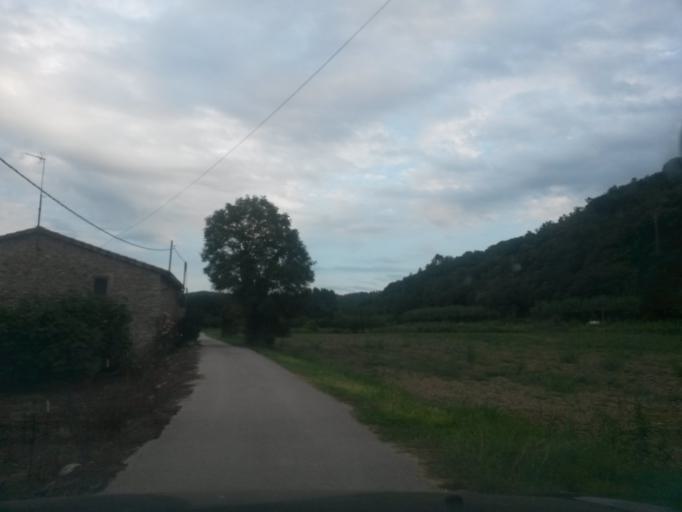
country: ES
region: Catalonia
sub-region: Provincia de Girona
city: Sant Gregori
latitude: 41.9741
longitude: 2.7148
